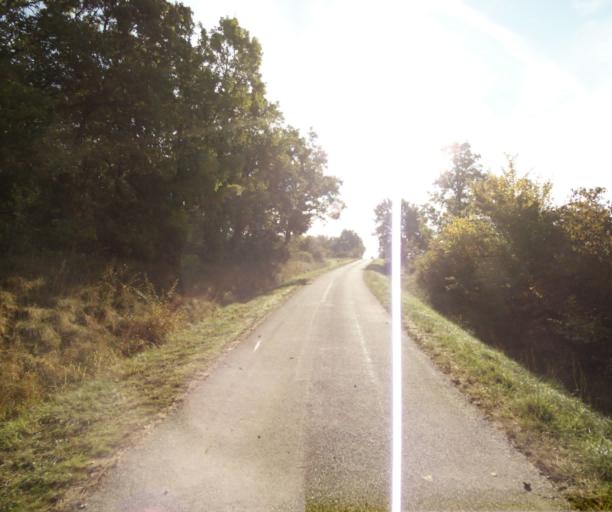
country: FR
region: Midi-Pyrenees
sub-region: Departement du Tarn-et-Garonne
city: Nohic
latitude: 43.9210
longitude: 1.4447
